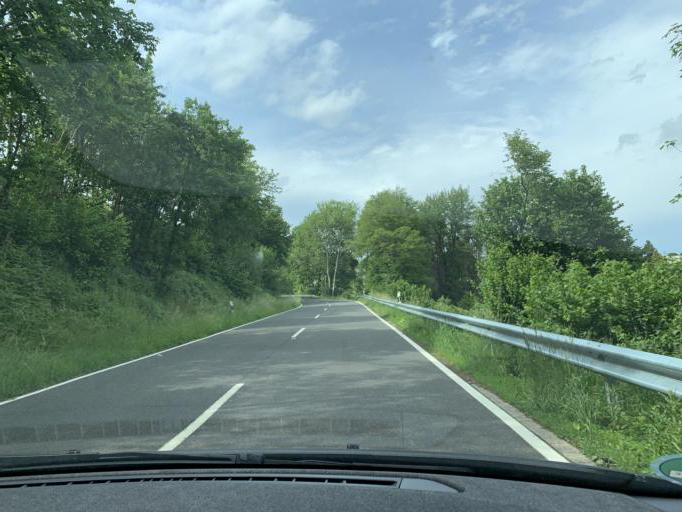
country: DE
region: North Rhine-Westphalia
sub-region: Regierungsbezirk Koln
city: Hurtgenwald
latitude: 50.6866
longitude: 6.3879
